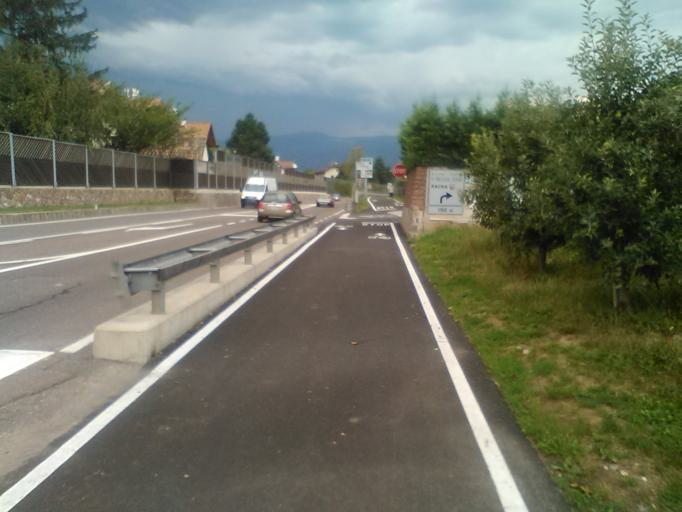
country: IT
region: Trentino-Alto Adige
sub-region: Bolzano
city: San Michele
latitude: 46.4499
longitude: 11.2654
